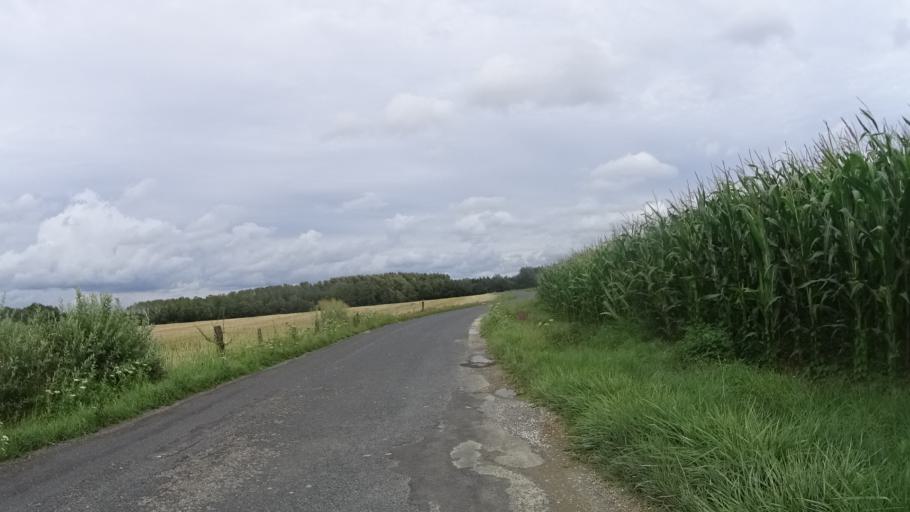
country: FR
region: Lorraine
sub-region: Departement de la Moselle
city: Sarrebourg
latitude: 48.6965
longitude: 7.0578
